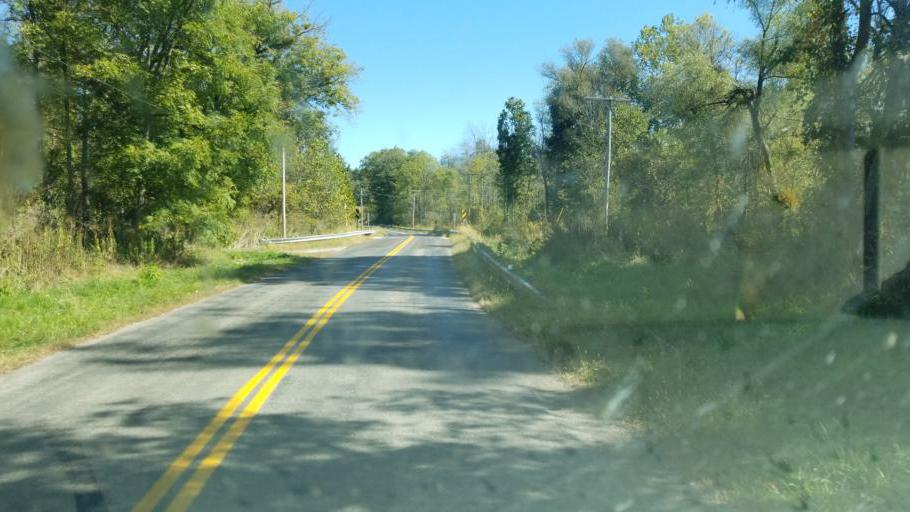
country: US
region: Ohio
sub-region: Huron County
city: New London
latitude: 40.9931
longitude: -82.3979
